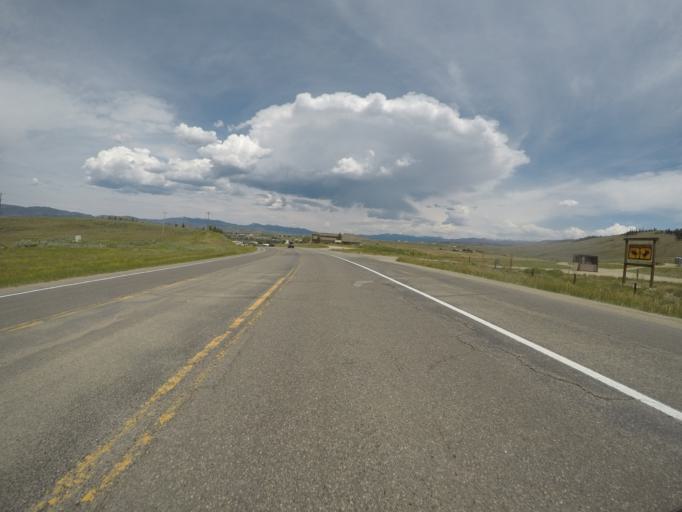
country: US
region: Colorado
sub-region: Grand County
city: Granby
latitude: 40.0661
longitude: -105.9247
